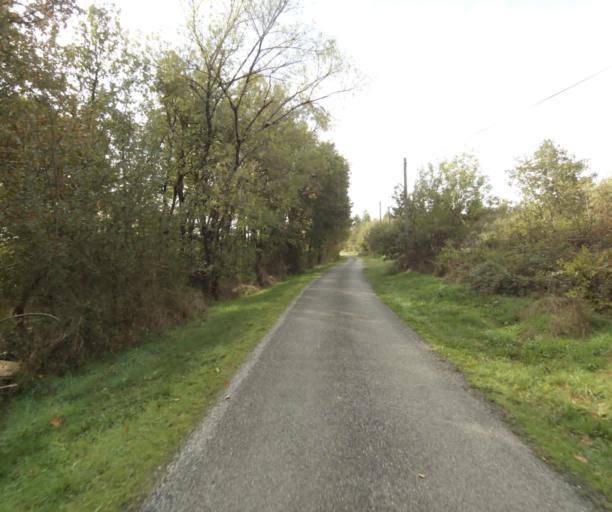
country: FR
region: Midi-Pyrenees
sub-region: Departement du Tarn-et-Garonne
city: Orgueil
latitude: 43.8894
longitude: 1.4134
